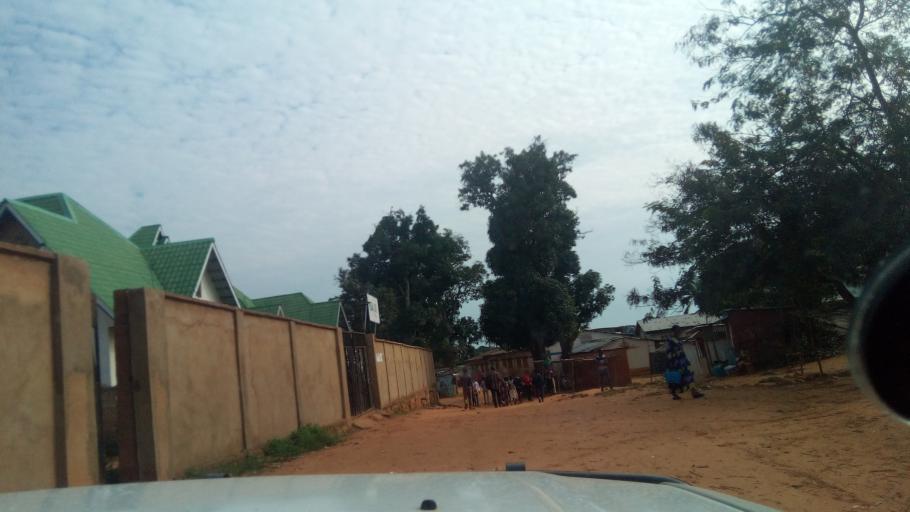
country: CD
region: Kasai-Oriental
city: Kabinda
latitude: -6.1348
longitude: 24.4874
